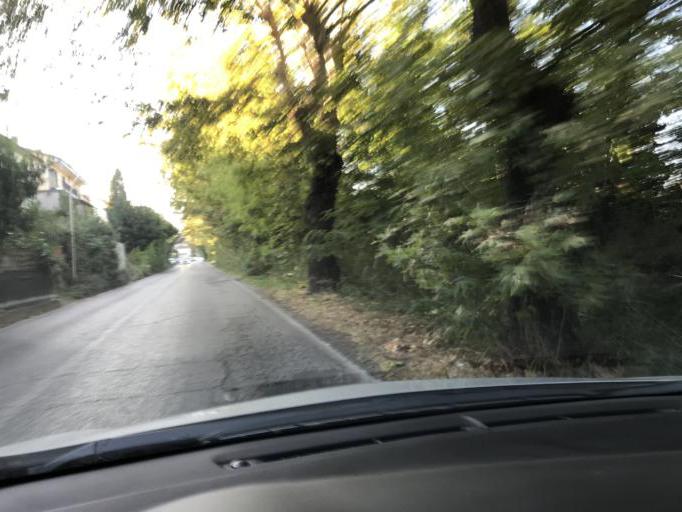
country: IT
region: Latium
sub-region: Provincia di Viterbo
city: Orte Scalo
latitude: 42.4444
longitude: 12.4006
